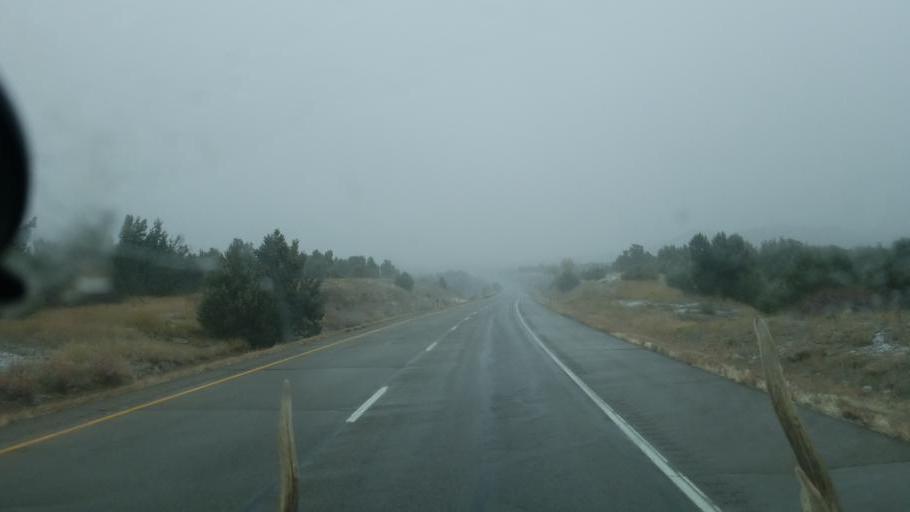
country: US
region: Colorado
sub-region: Pueblo County
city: Colorado City
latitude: 38.0429
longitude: -104.7275
